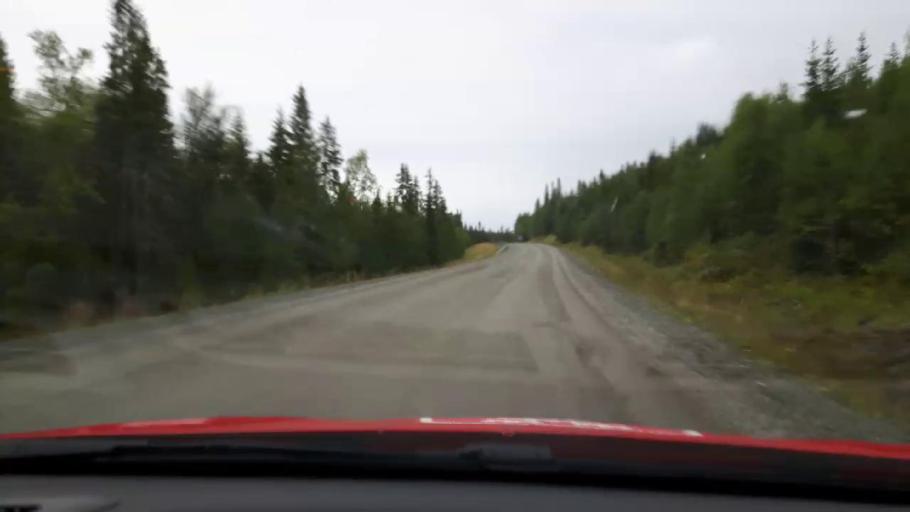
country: SE
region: Jaemtland
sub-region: Are Kommun
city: Are
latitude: 63.4371
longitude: 12.7222
